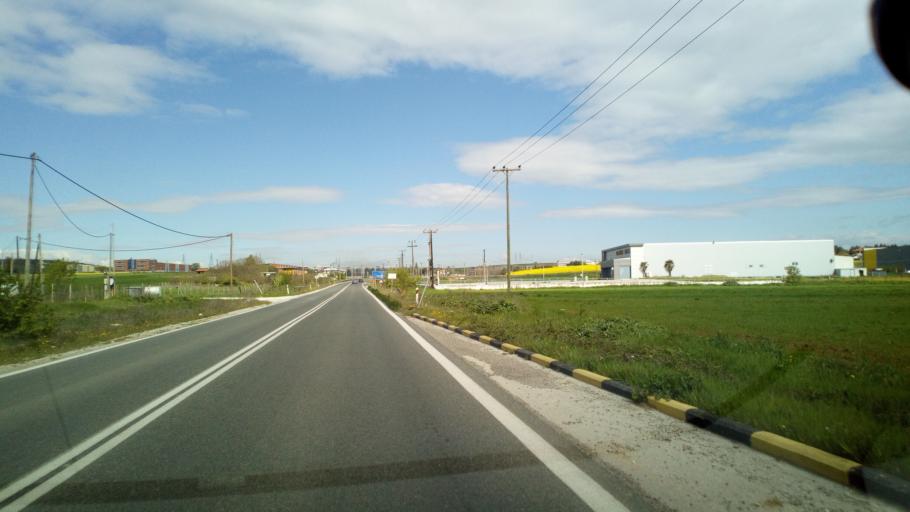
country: GR
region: Central Macedonia
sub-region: Nomos Thessalonikis
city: Drymos
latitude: 40.7720
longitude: 22.9495
